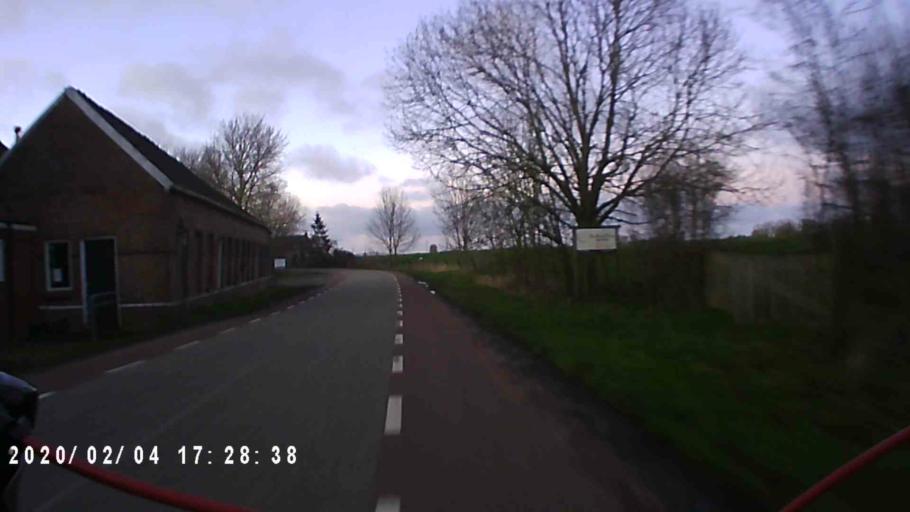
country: NL
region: Groningen
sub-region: Gemeente Zuidhorn
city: Aduard
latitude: 53.2702
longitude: 6.5062
